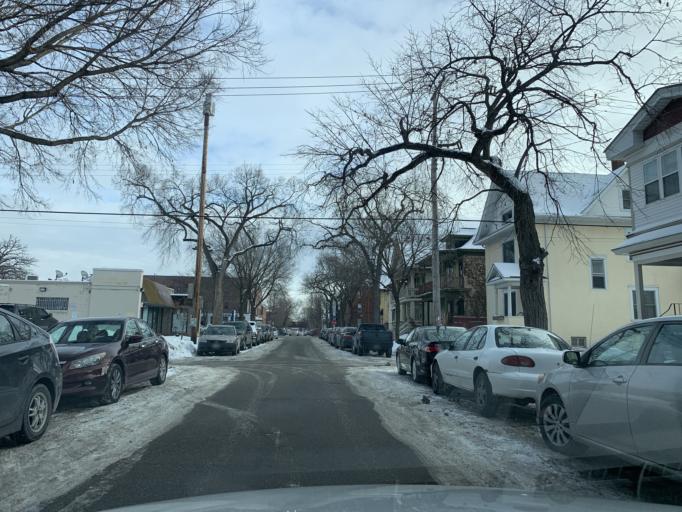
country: US
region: Minnesota
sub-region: Hennepin County
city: Minneapolis
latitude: 44.9573
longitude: -93.2791
